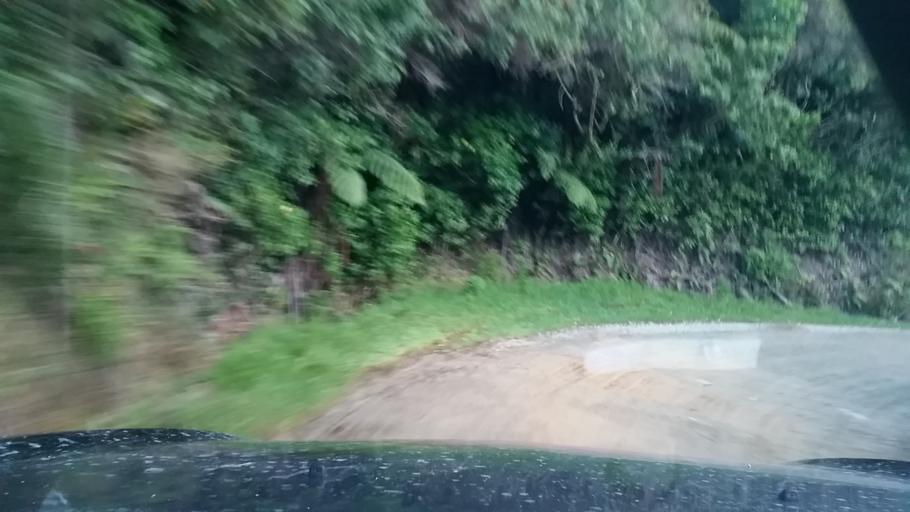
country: NZ
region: Marlborough
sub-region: Marlborough District
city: Picton
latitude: -41.1382
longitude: 174.1415
